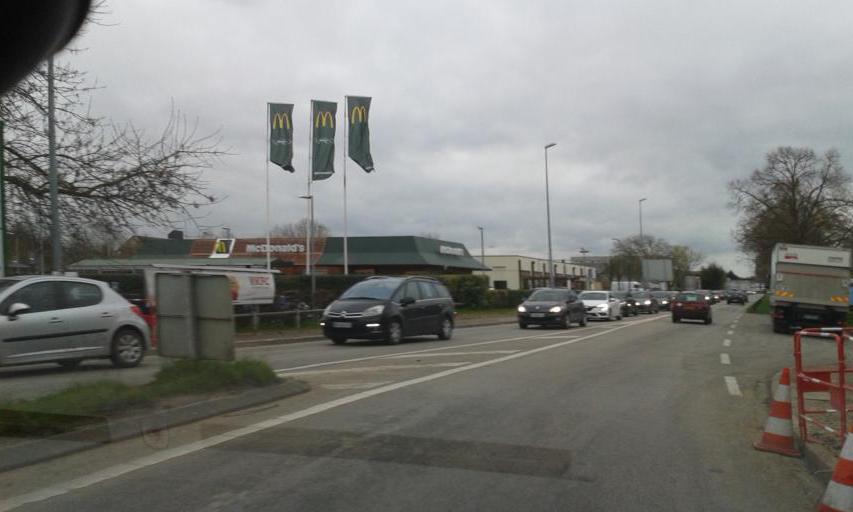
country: FR
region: Centre
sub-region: Departement d'Eure-et-Loir
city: Le Coudray
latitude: 48.4279
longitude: 1.5146
